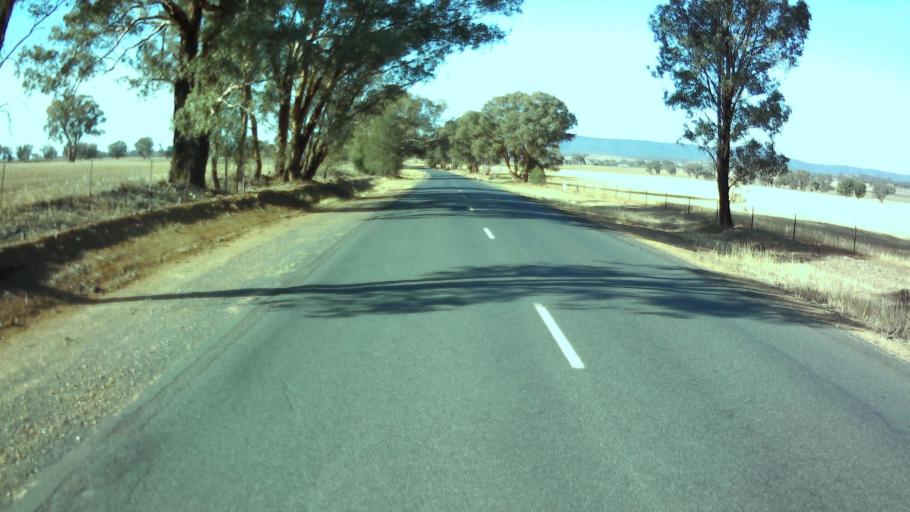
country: AU
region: New South Wales
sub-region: Weddin
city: Grenfell
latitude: -33.9217
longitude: 148.1400
